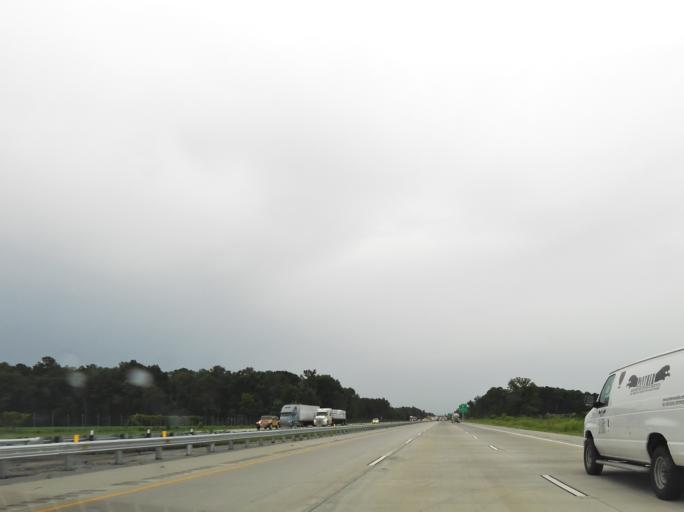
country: US
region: Georgia
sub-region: Dooly County
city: Vienna
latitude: 32.1426
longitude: -83.7577
